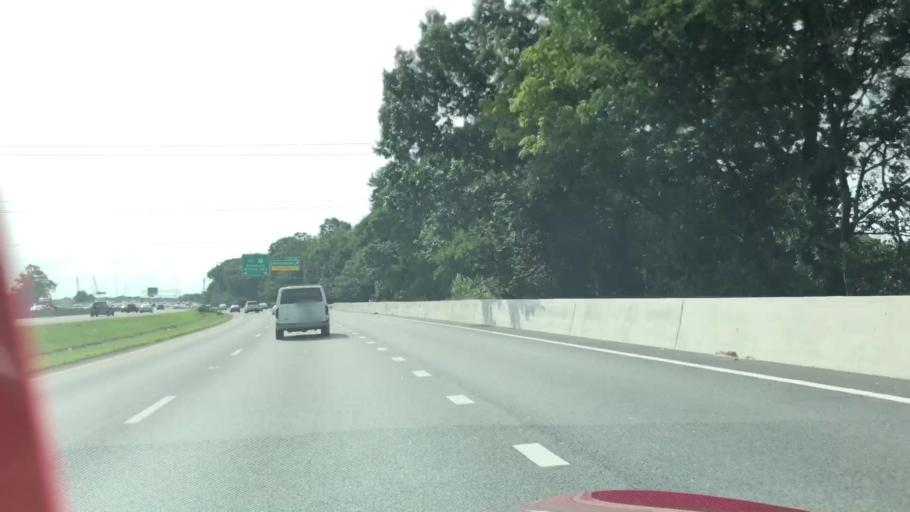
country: US
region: Virginia
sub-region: City of Chesapeake
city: Chesapeake
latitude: 36.8460
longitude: -76.1747
